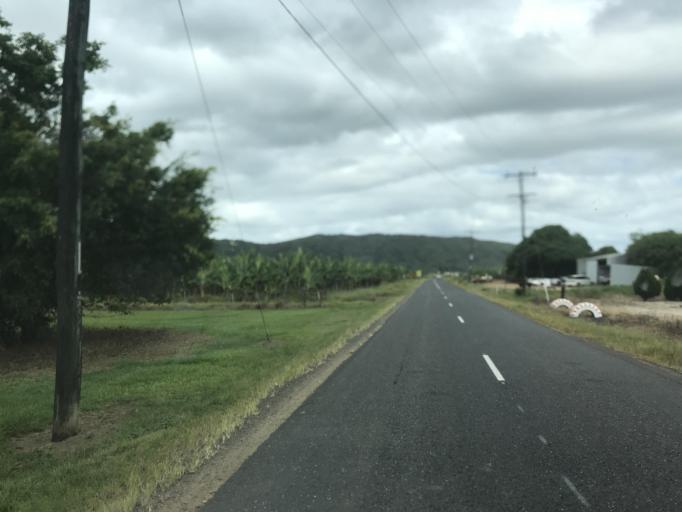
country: AU
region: Queensland
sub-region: Cassowary Coast
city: Innisfail
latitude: -17.6208
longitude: 146.0214
